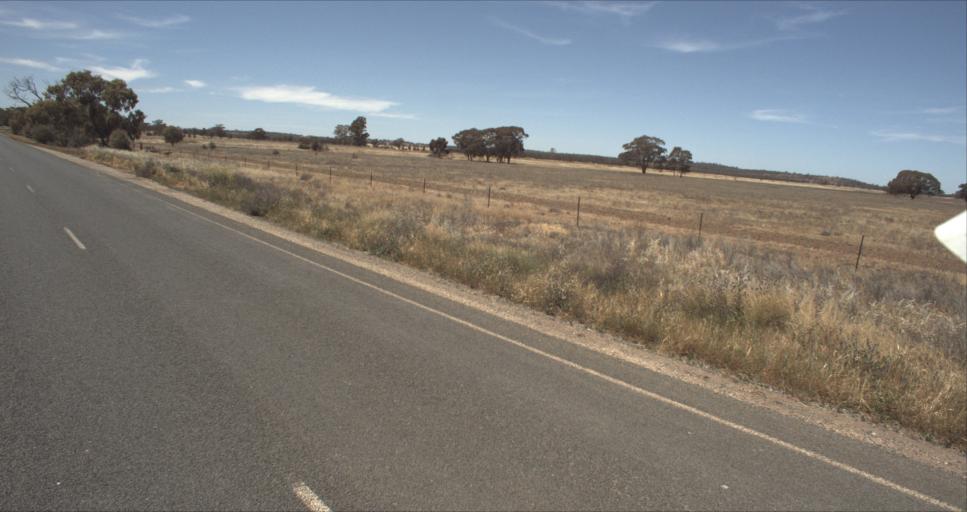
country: AU
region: New South Wales
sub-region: Leeton
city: Leeton
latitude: -34.6504
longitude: 146.4668
